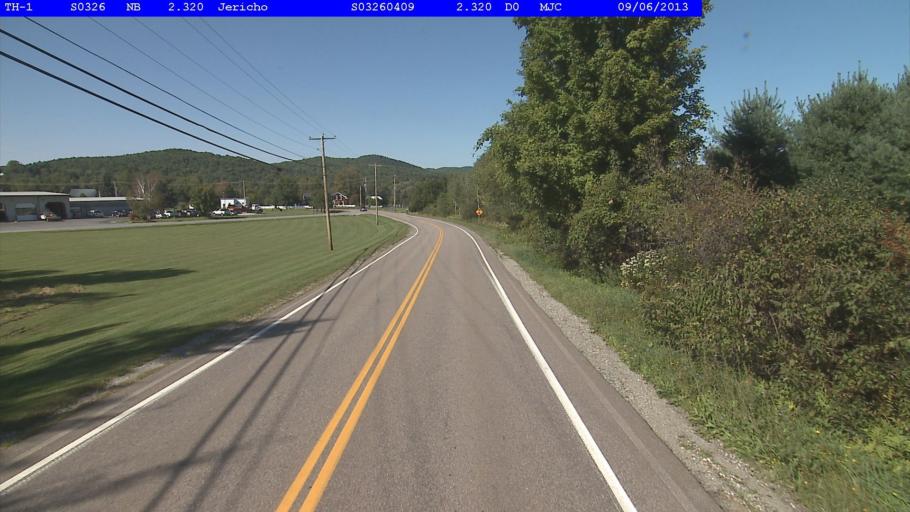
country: US
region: Vermont
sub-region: Chittenden County
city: Jericho
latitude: 44.5098
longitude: -72.9540
